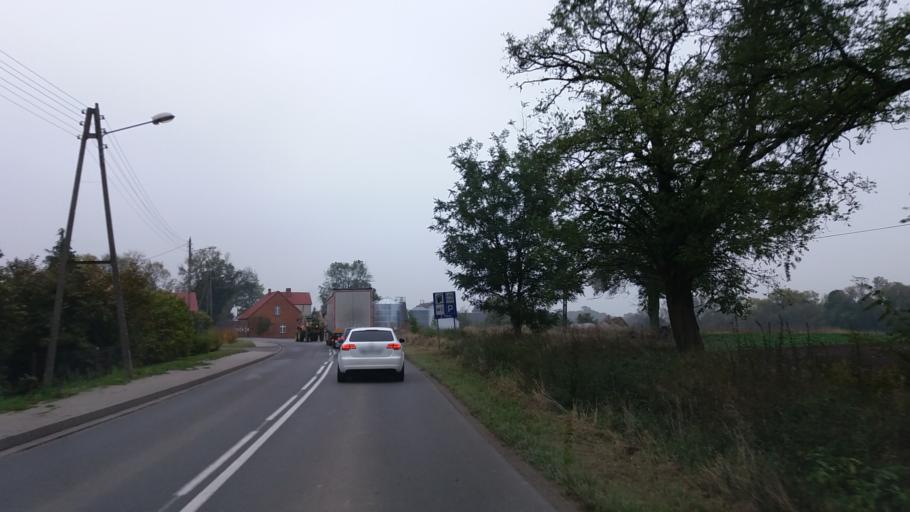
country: PL
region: West Pomeranian Voivodeship
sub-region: Powiat choszczenski
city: Bierzwnik
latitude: 53.0469
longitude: 15.6662
